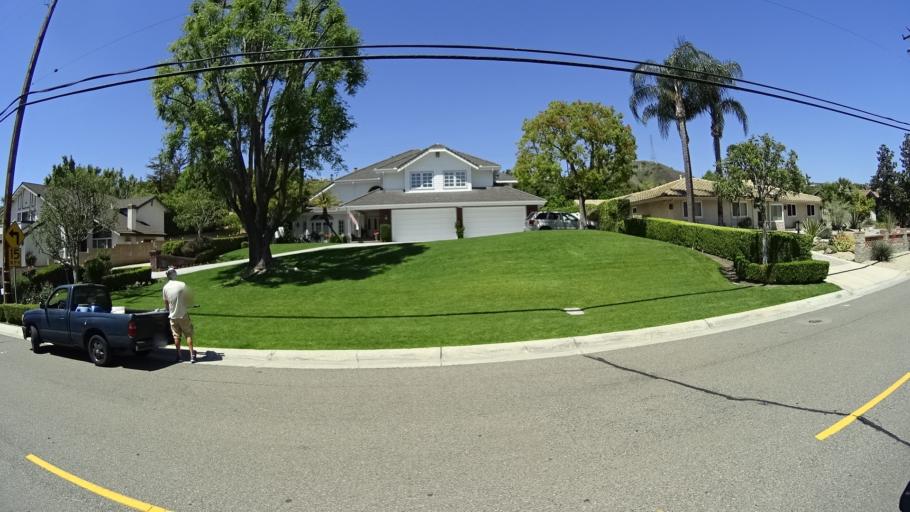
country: US
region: California
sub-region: Orange County
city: Villa Park
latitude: 33.8266
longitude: -117.8060
